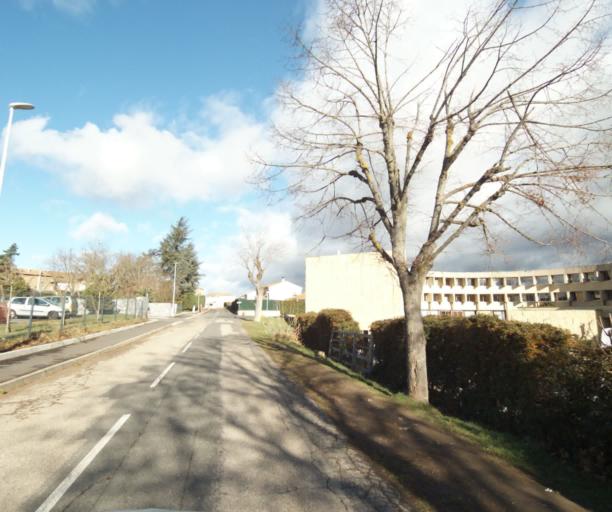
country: FR
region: Rhone-Alpes
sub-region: Departement de la Loire
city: La Talaudiere
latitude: 45.4672
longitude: 4.4166
